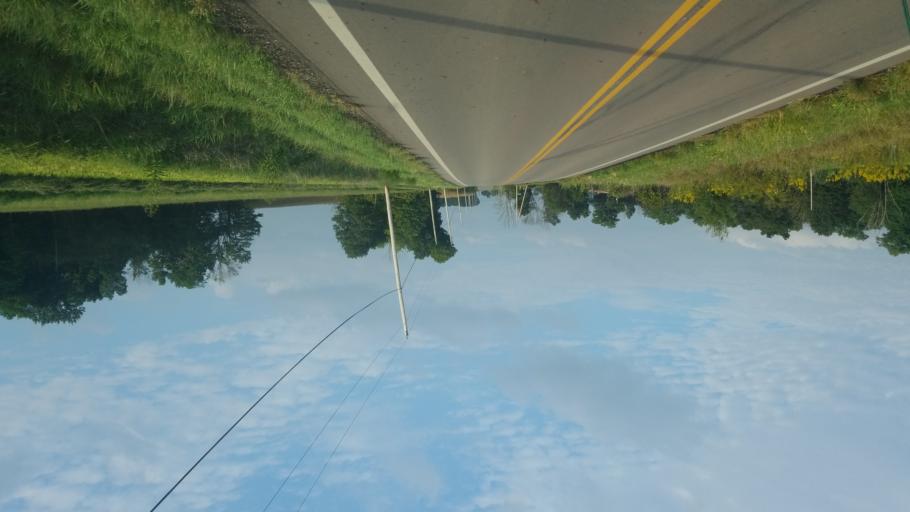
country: US
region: Ohio
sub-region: Wayne County
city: Wooster
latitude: 40.8524
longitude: -82.0352
